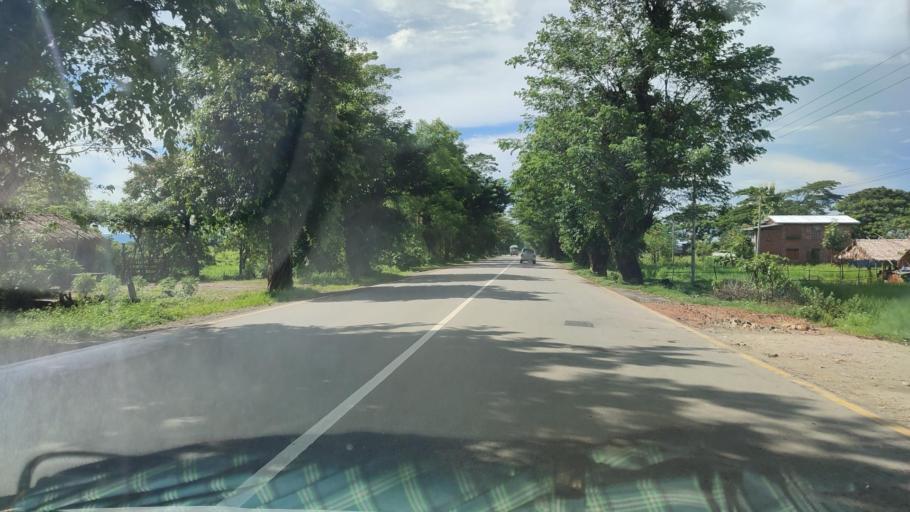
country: MM
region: Bago
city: Pyu
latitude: 18.2613
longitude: 96.5288
